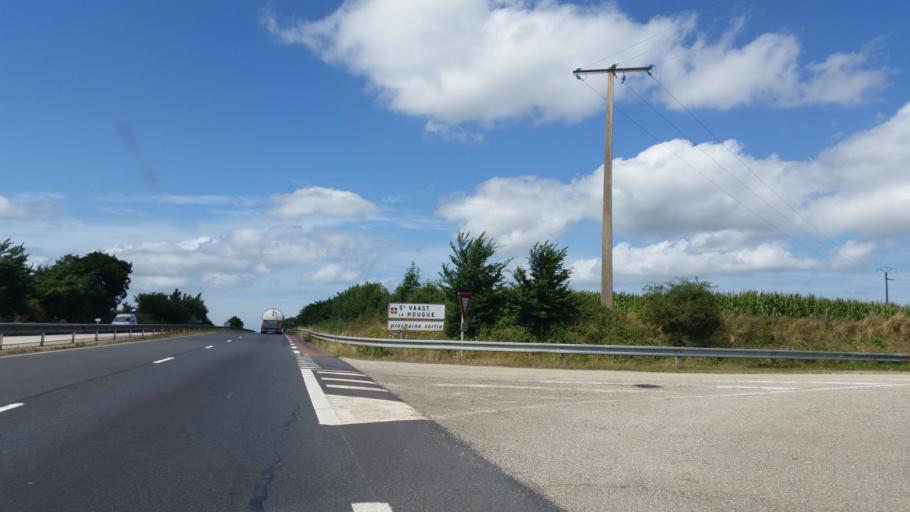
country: FR
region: Lower Normandy
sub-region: Departement de la Manche
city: Montebourg
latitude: 49.4531
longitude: -1.3519
